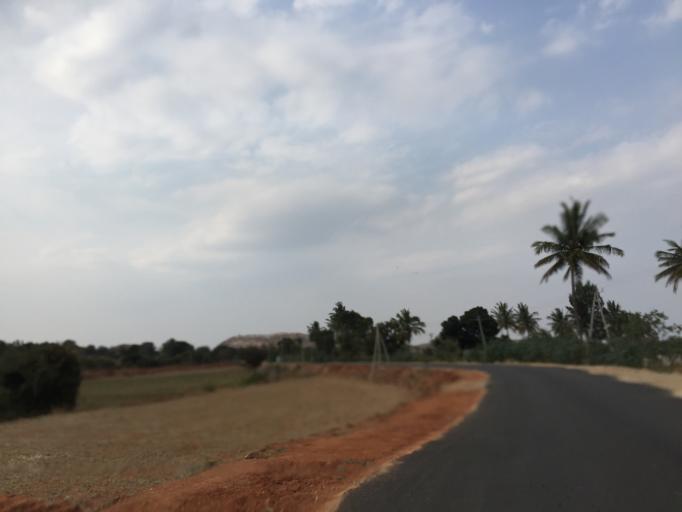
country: IN
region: Karnataka
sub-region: Chikkaballapur
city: Gudibanda
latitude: 13.5592
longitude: 77.7379
